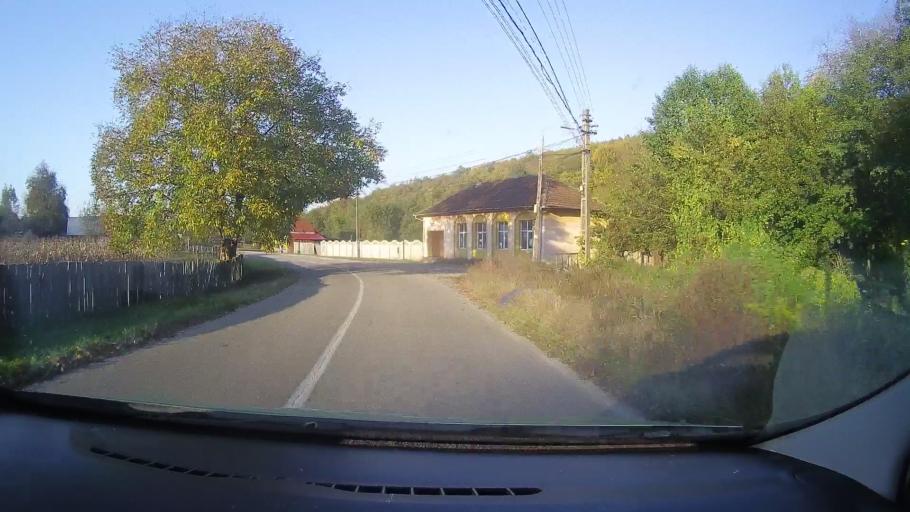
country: RO
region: Timis
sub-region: Comuna Fardea
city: Fardea
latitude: 45.7165
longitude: 22.1583
